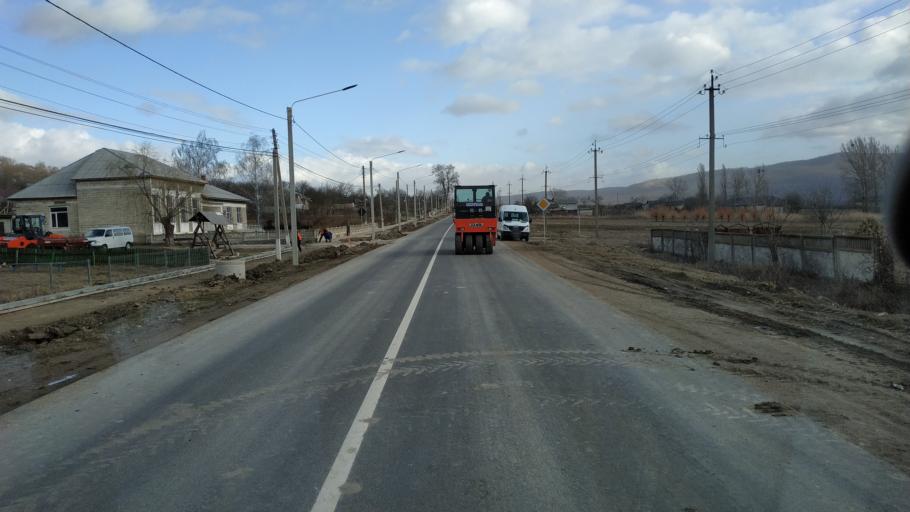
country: MD
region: Calarasi
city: Calarasi
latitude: 47.3198
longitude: 28.1104
